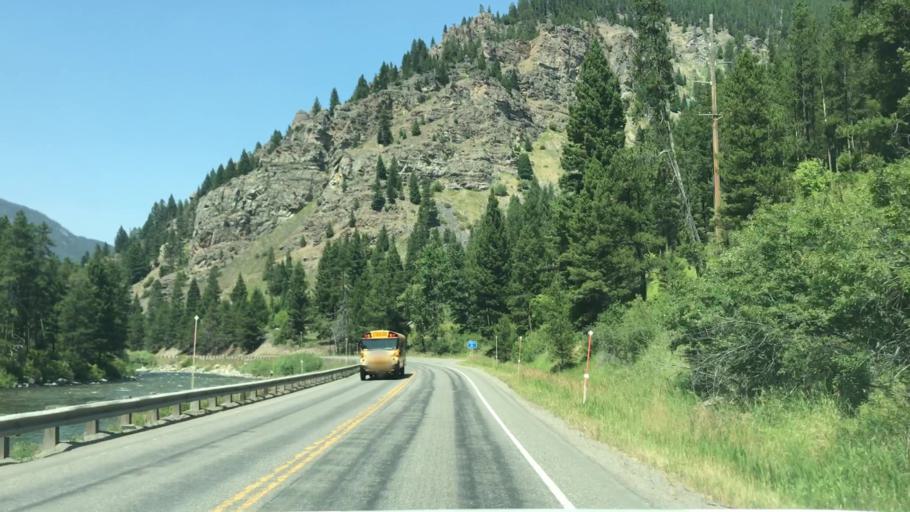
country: US
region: Montana
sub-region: Gallatin County
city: Big Sky
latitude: 45.3938
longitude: -111.2059
